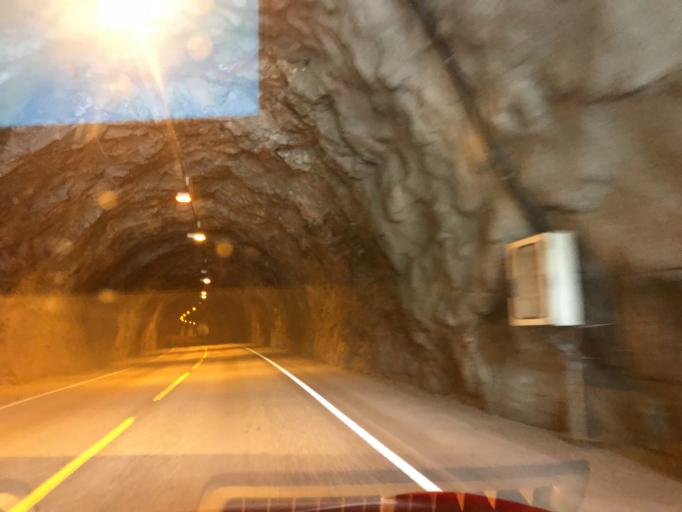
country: NO
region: Hordaland
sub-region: Eidfjord
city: Eidfjord
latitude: 60.4518
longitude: 7.0932
